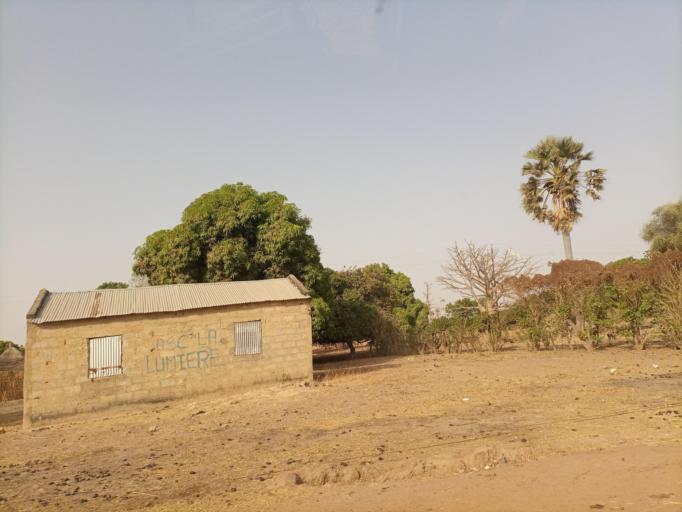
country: SN
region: Fatick
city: Passi
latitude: 14.0187
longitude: -16.2941
